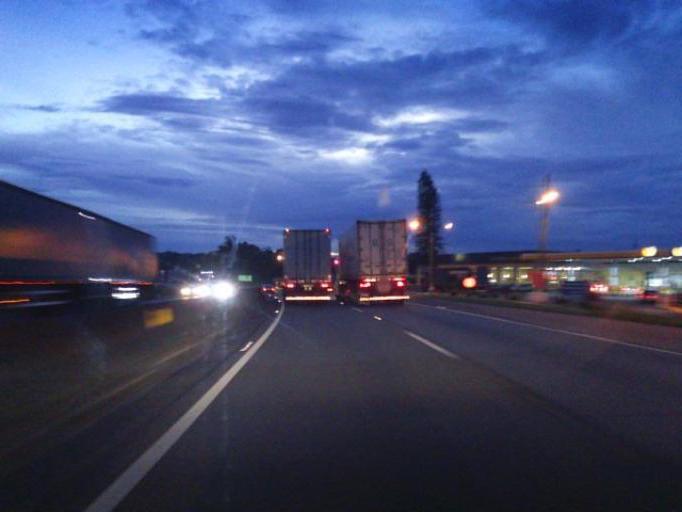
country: BR
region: Santa Catarina
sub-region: Barra Velha
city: Barra Velha
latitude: -26.5541
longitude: -48.7194
